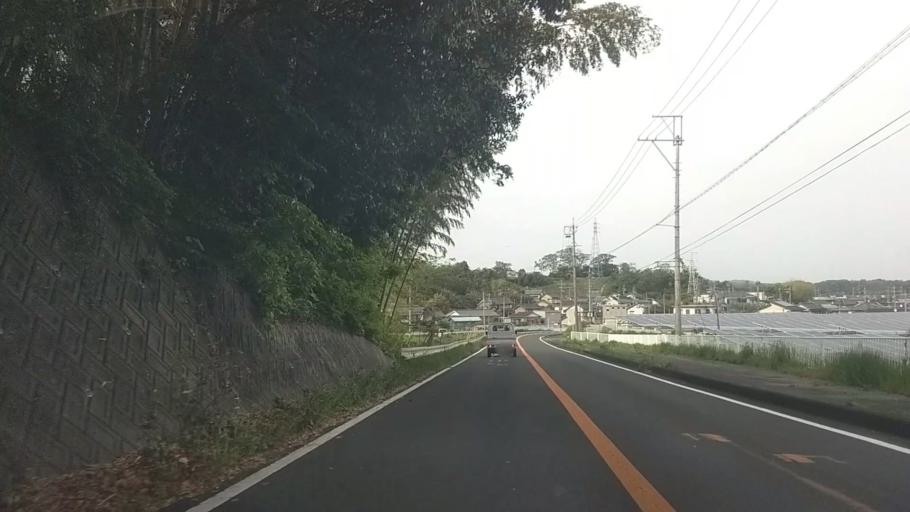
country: JP
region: Shizuoka
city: Kosai-shi
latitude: 34.7366
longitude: 137.6004
